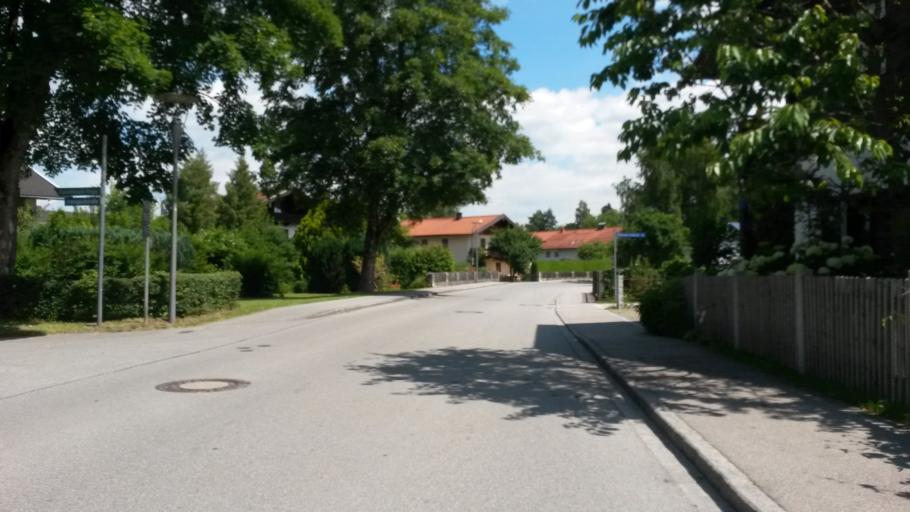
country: DE
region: Bavaria
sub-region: Upper Bavaria
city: Chieming
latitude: 47.8911
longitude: 12.5349
